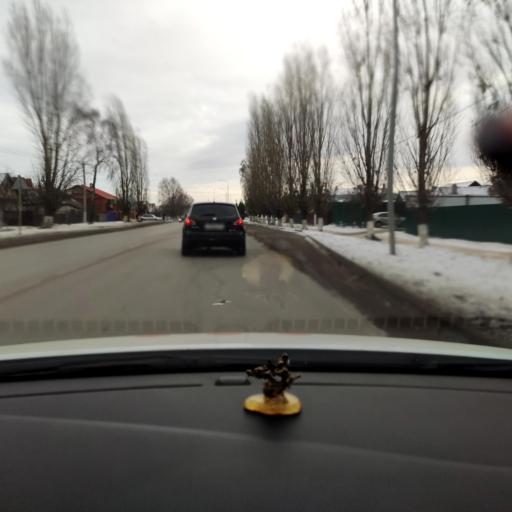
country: RU
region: Tatarstan
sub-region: Zelenodol'skiy Rayon
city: Zelenodolsk
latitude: 55.8477
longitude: 48.5312
